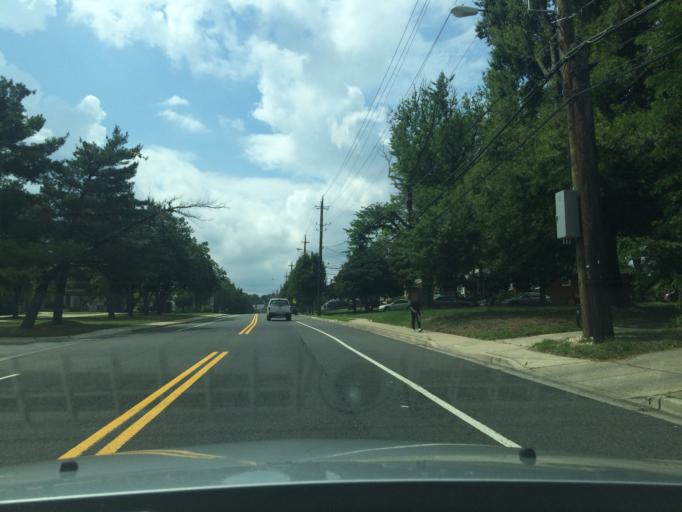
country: US
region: Maryland
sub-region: Prince George's County
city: Suitland
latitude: 38.8559
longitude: -76.9207
